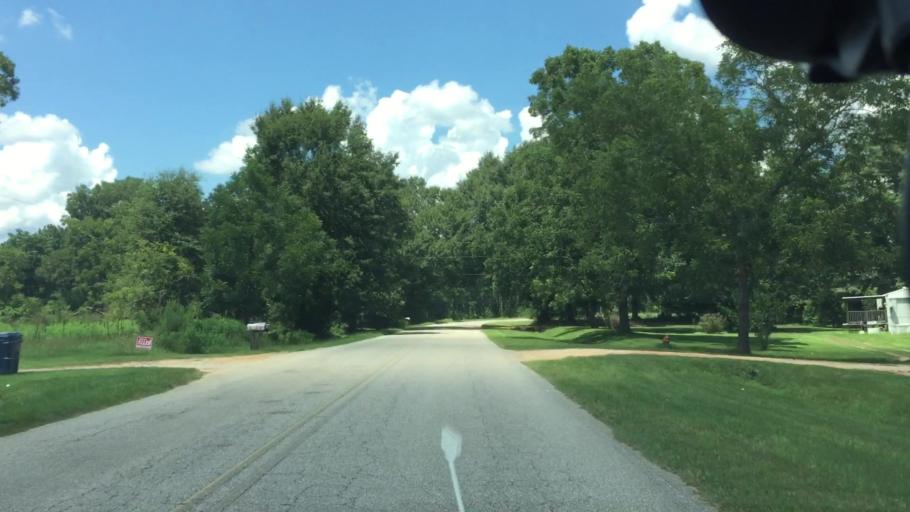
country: US
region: Alabama
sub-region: Pike County
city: Troy
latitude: 31.7526
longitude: -85.9845
